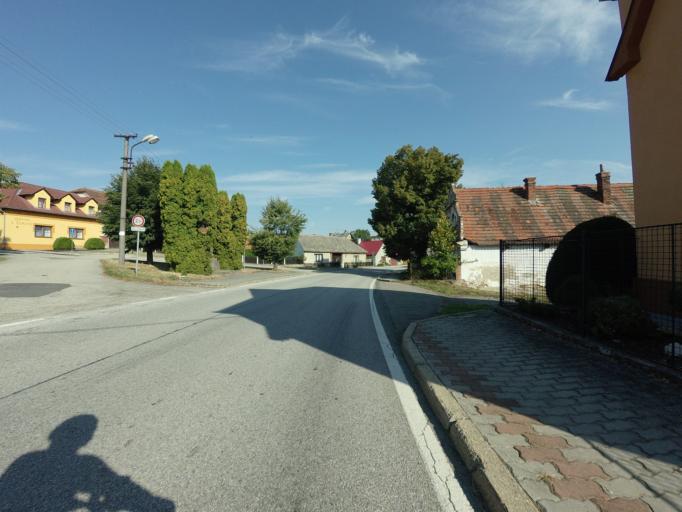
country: CZ
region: Jihocesky
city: Bernartice
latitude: 49.2945
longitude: 14.3885
